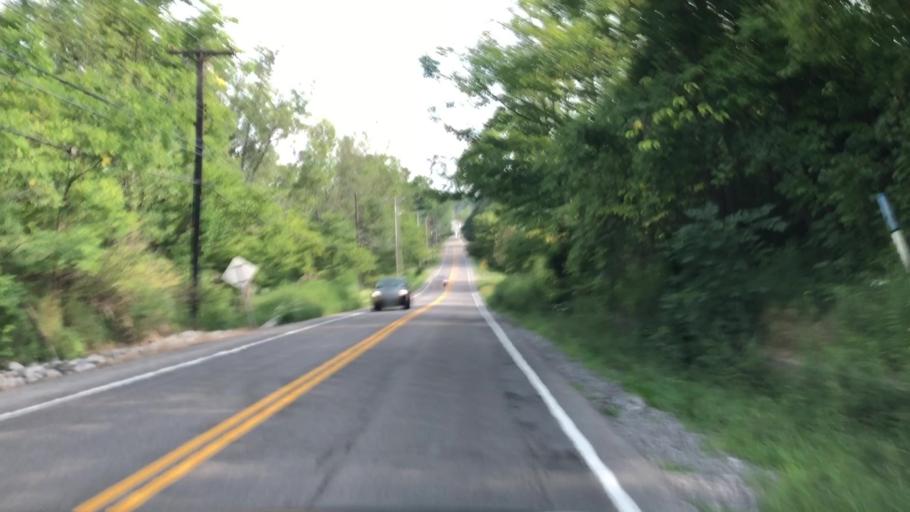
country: US
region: New York
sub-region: Erie County
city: Elma Center
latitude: 42.8534
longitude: -78.6403
